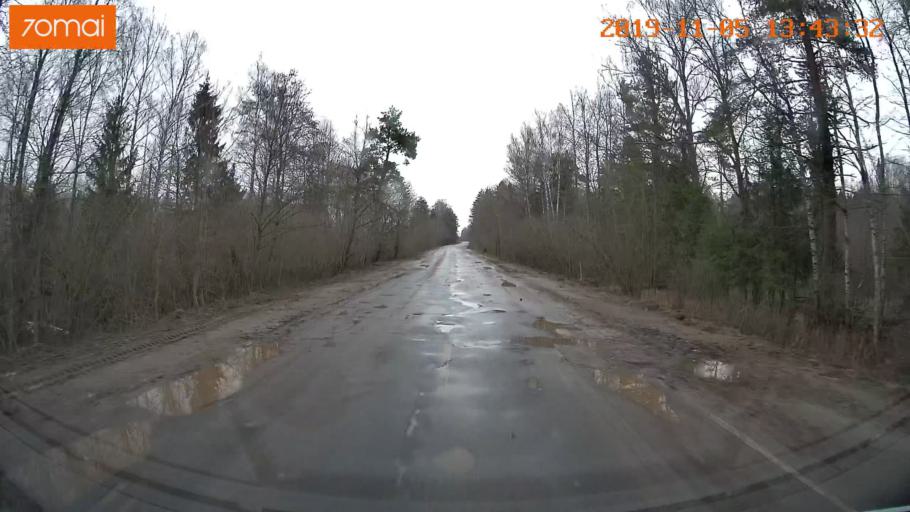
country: RU
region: Ivanovo
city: Shuya
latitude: 56.9742
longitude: 41.4037
